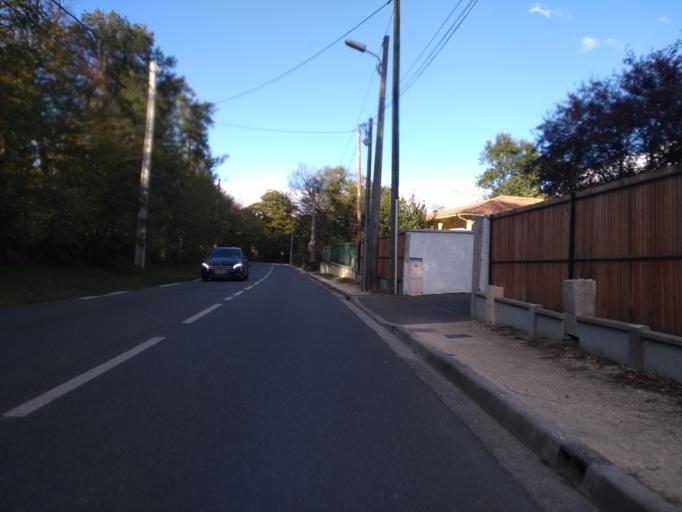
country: FR
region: Aquitaine
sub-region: Departement de la Gironde
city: Gradignan
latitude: 44.7603
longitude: -0.6146
